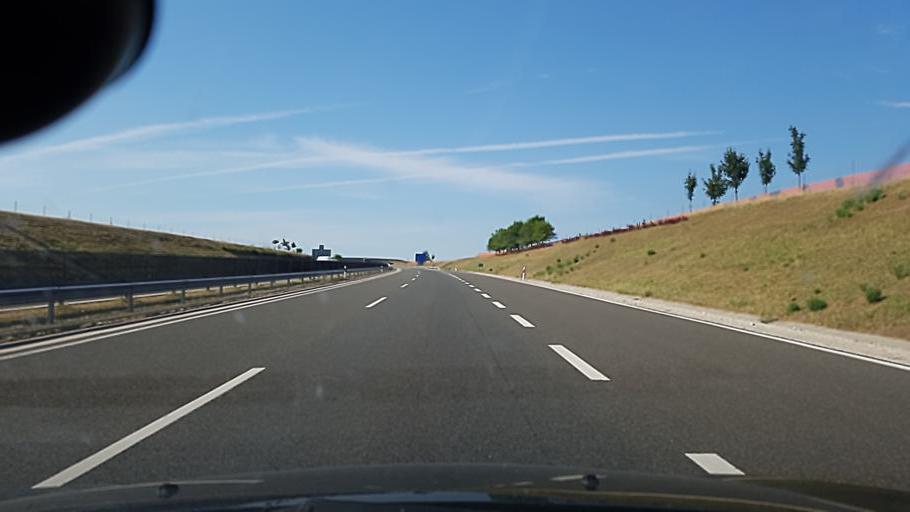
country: HU
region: Tolna
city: Paks
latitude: 46.6676
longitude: 18.8134
